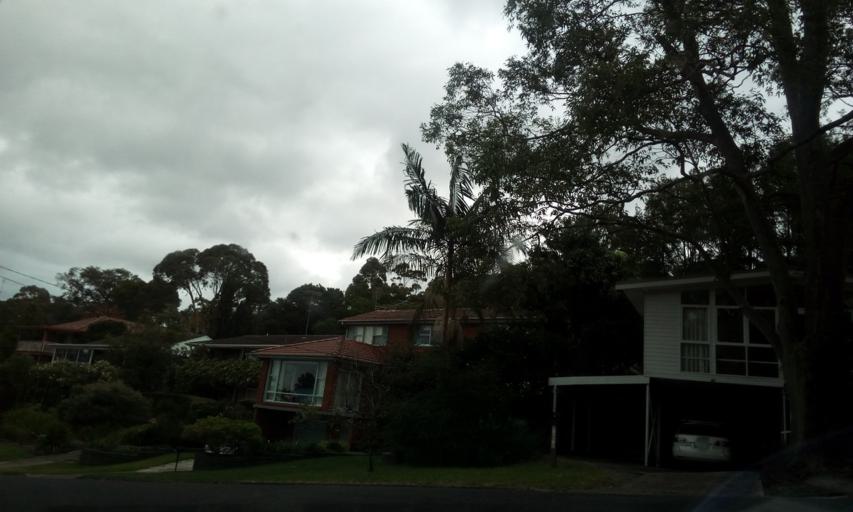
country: AU
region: New South Wales
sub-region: Wollongong
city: Keiraville
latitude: -34.4107
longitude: 150.8662
